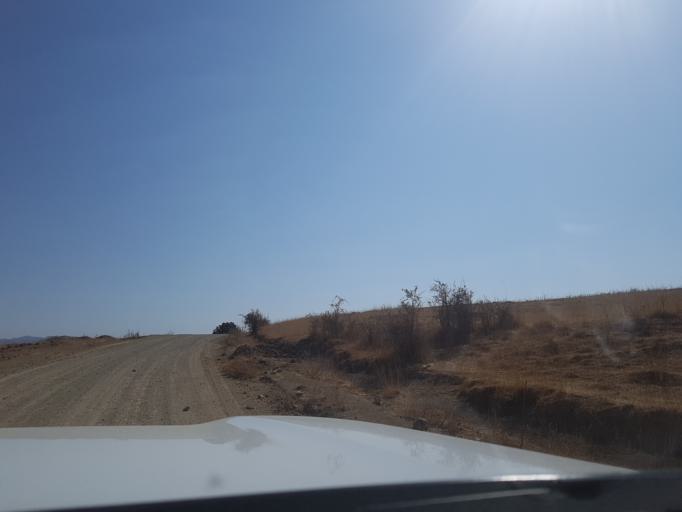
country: TM
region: Ahal
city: Baharly
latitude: 38.3607
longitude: 56.8791
